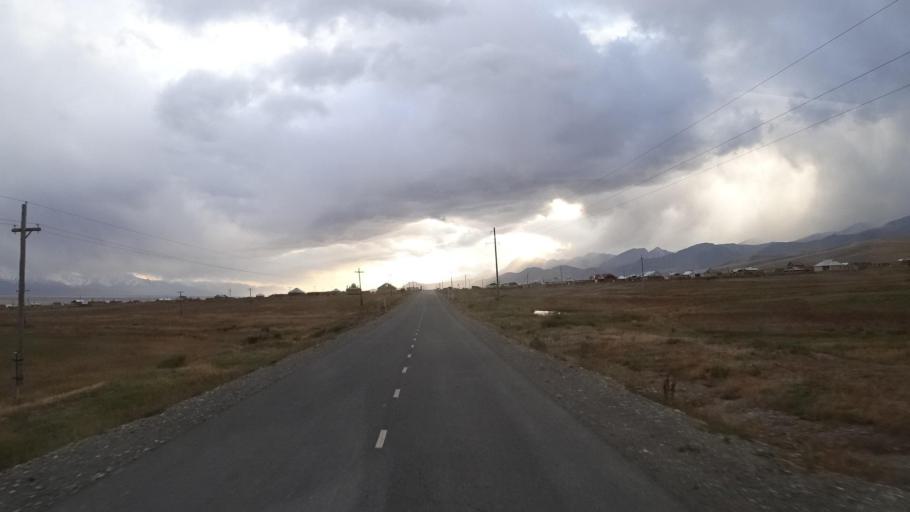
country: KG
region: Osh
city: Gul'cha
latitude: 39.6784
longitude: 72.8955
